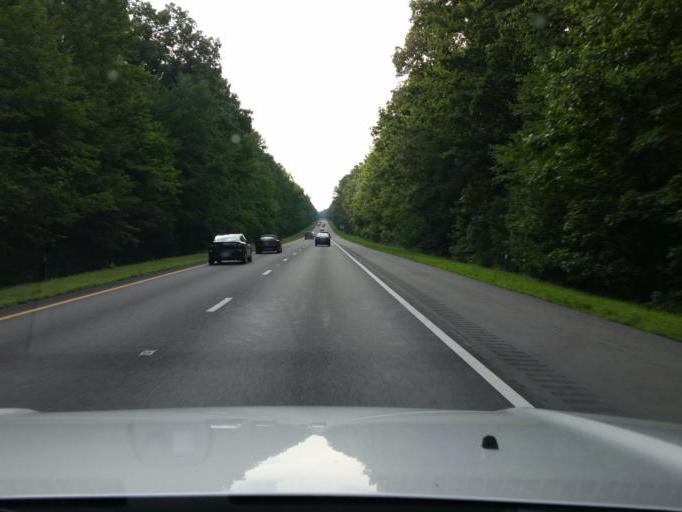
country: US
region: Virginia
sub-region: King William County
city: West Point
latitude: 37.4309
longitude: -76.8416
